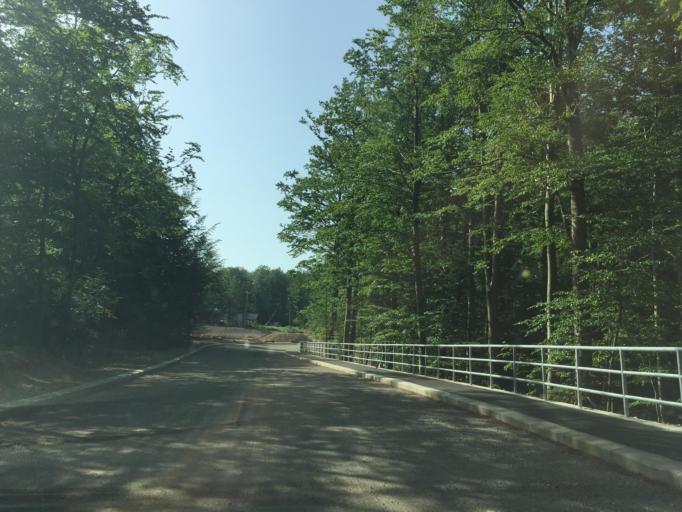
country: HR
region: Primorsko-Goranska
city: Podhum
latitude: 45.4280
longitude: 14.5659
